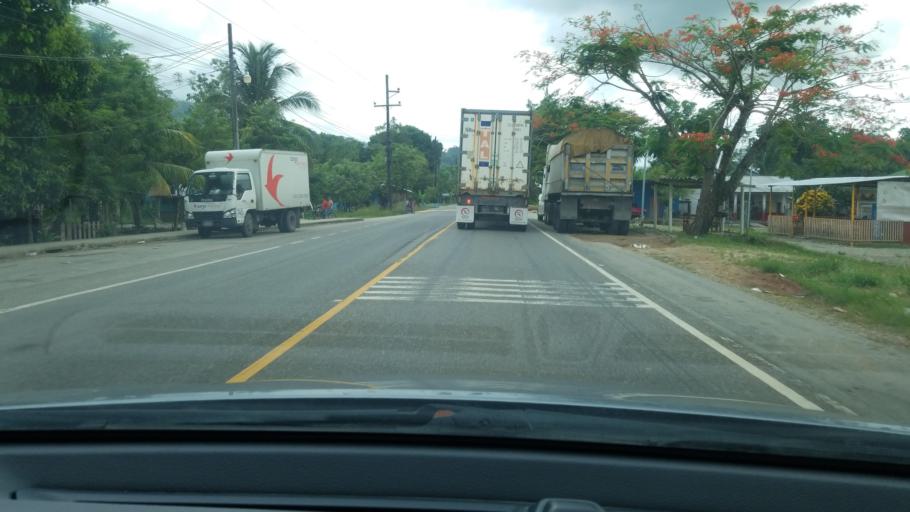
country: HN
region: Cortes
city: Potrerillos
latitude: 15.5920
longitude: -88.3247
